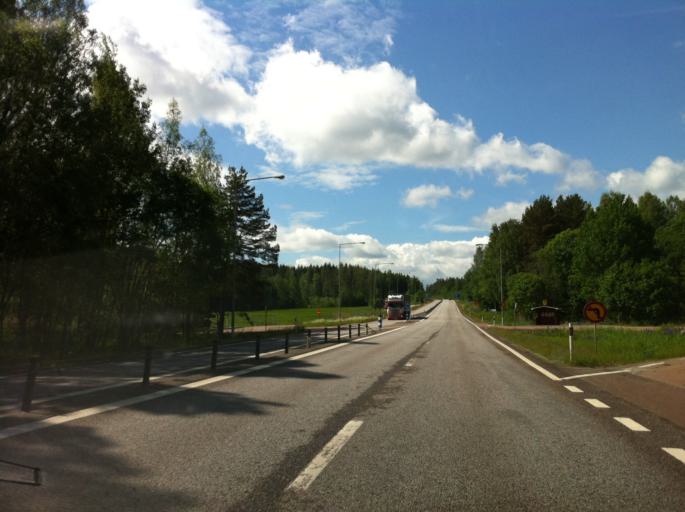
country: SE
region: Vaermland
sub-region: Grums Kommun
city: Slottsbron
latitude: 59.3093
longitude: 13.0841
